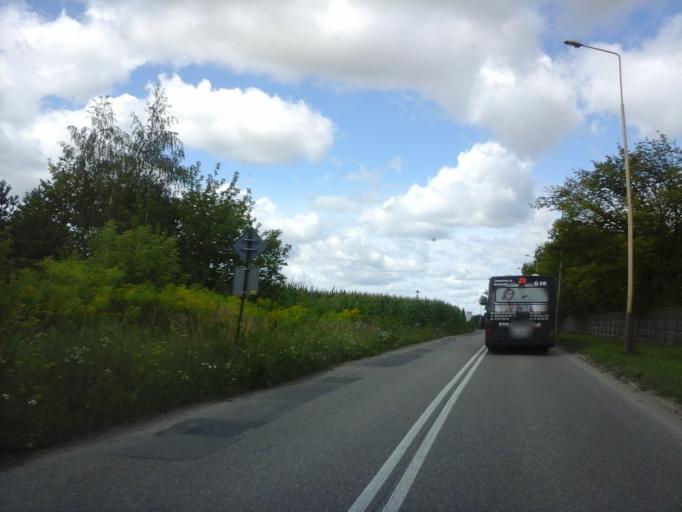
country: PL
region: West Pomeranian Voivodeship
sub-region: Powiat pyrzycki
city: Warnice
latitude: 53.3007
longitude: 15.0033
